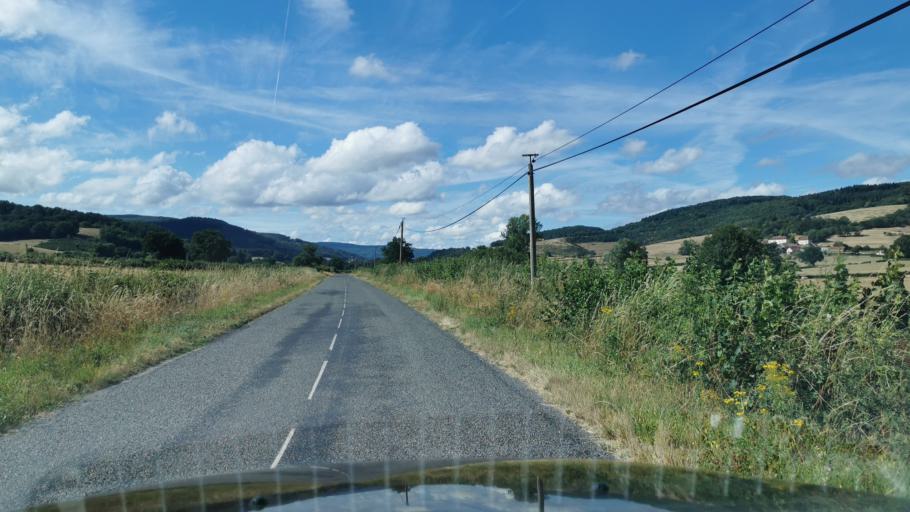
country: FR
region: Bourgogne
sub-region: Departement de Saone-et-Loire
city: Marmagne
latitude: 46.8101
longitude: 4.3283
